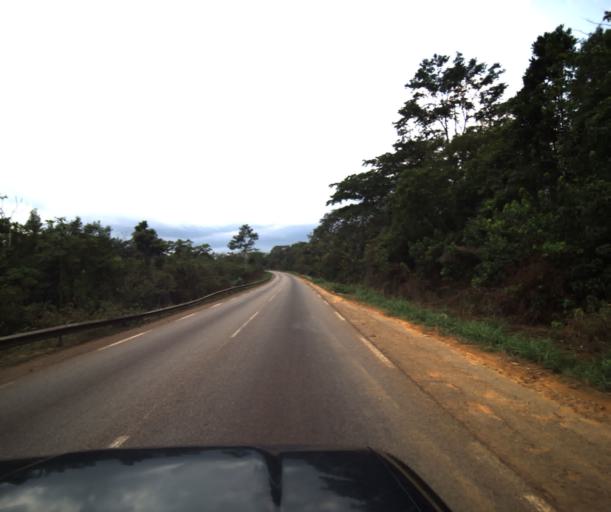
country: CM
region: Littoral
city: Edea
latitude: 3.9423
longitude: 10.0462
